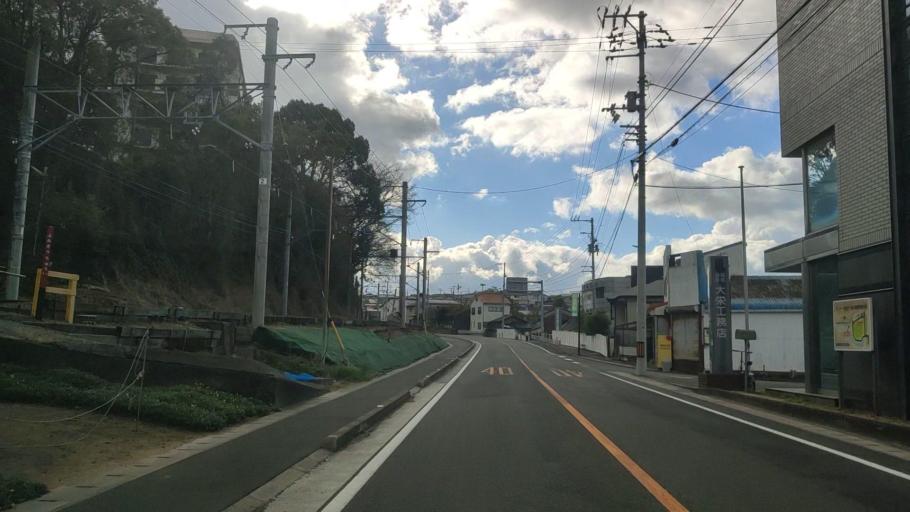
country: JP
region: Ehime
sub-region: Shikoku-chuo Shi
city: Matsuyama
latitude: 33.8815
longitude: 132.7020
